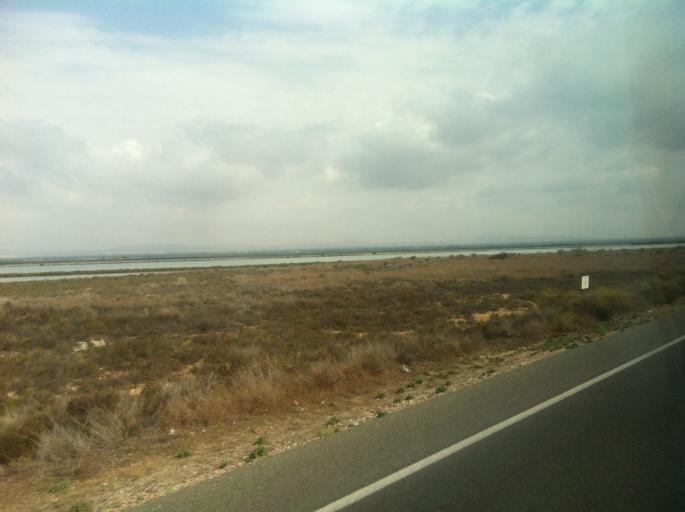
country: ES
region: Valencia
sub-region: Provincia de Alicante
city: Santa Pola
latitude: 38.1683
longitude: -0.6286
